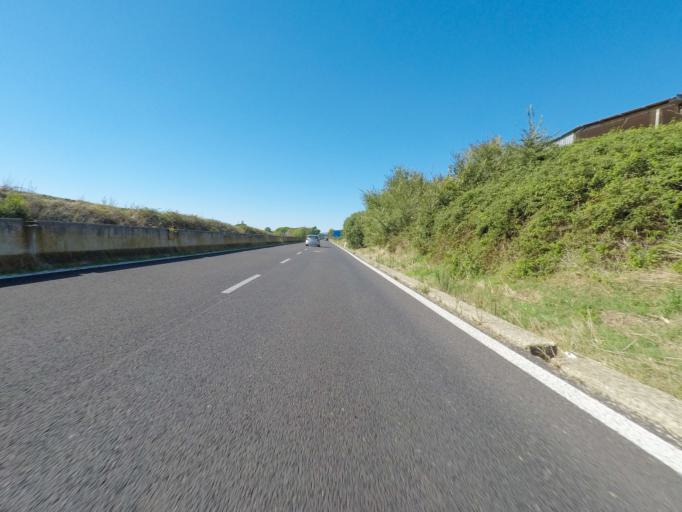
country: IT
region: Latium
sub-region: Provincia di Viterbo
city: Pescia Romana
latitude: 42.4003
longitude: 11.5071
